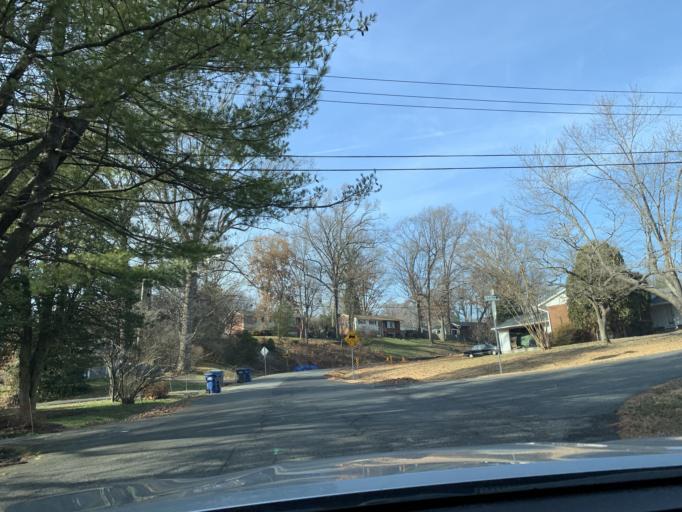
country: US
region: Virginia
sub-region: Fairfax County
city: Jefferson
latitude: 38.8489
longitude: -77.1847
